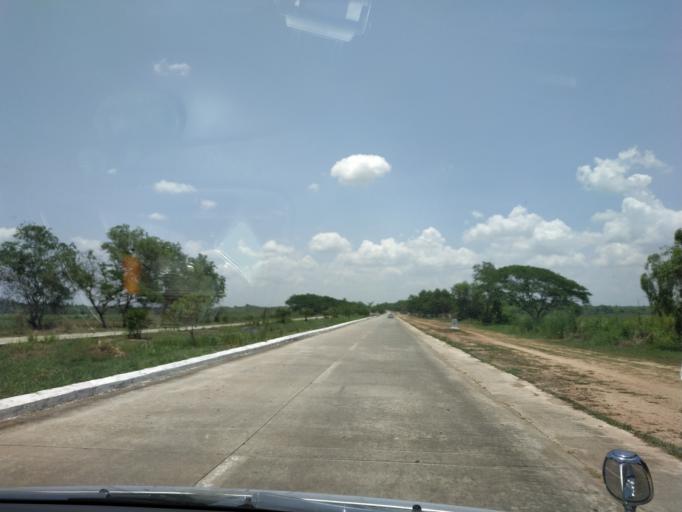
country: MM
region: Bago
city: Bago
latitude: 17.4257
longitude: 96.3747
